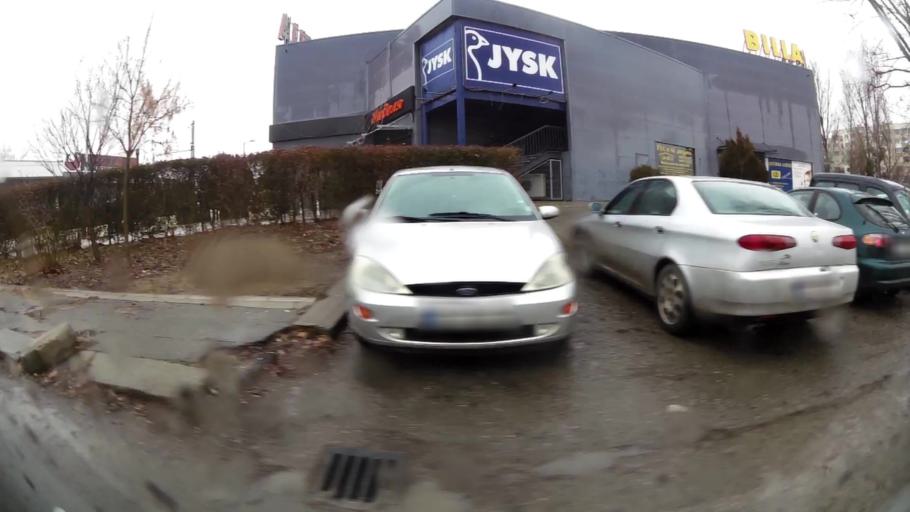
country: BG
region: Sofia-Capital
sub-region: Stolichna Obshtina
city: Sofia
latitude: 42.6422
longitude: 23.4082
